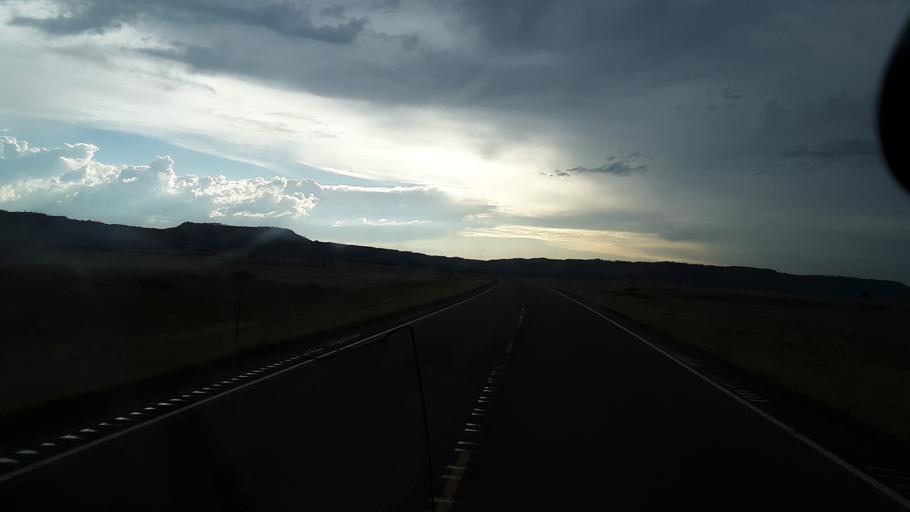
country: US
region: Montana
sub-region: Rosebud County
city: Lame Deer
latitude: 45.6128
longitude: -106.3617
